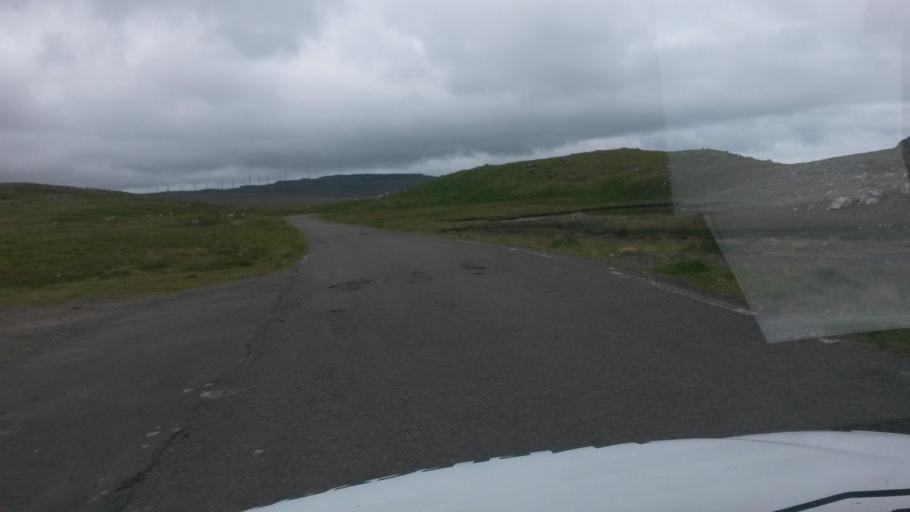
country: FO
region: Streymoy
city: Argir
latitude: 61.9935
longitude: -6.8484
